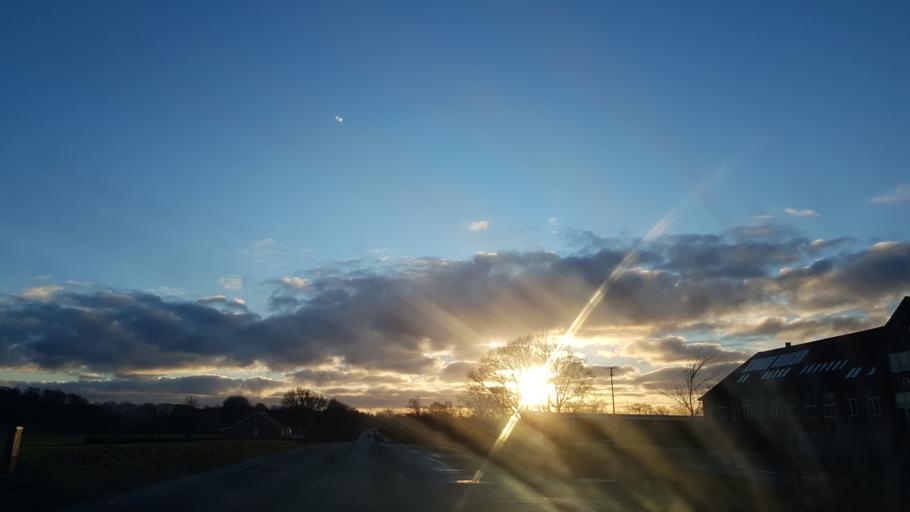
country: DK
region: South Denmark
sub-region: Kolding Kommune
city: Vamdrup
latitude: 55.4025
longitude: 9.3784
